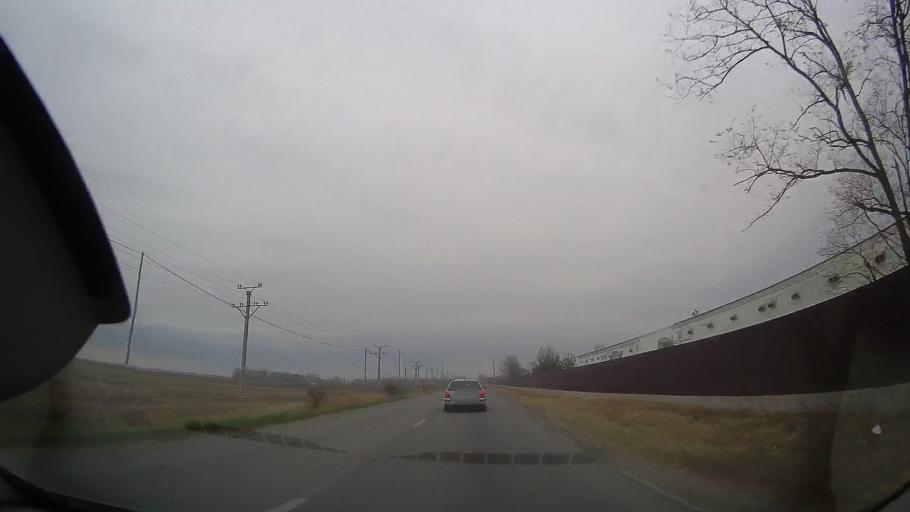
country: RO
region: Ialomita
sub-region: Oras Amara
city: Amara
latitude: 44.5873
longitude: 27.3323
